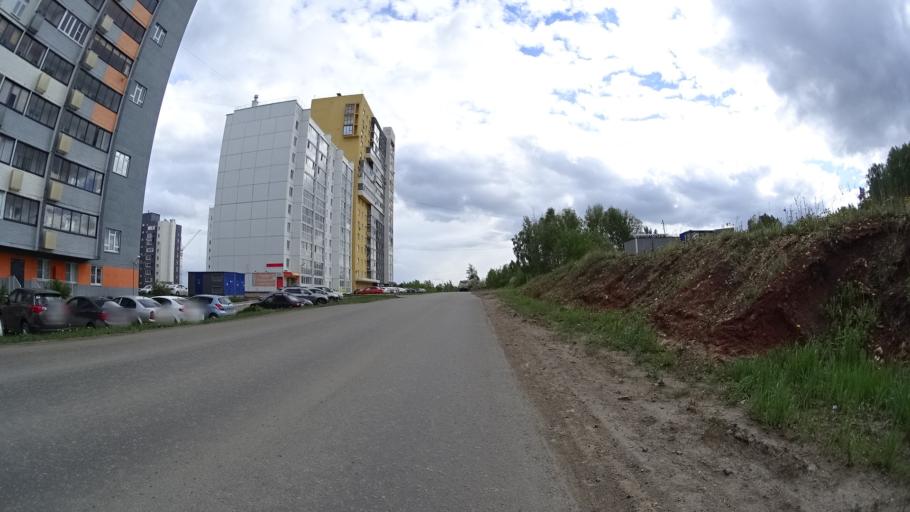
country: RU
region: Chelyabinsk
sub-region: Gorod Chelyabinsk
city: Chelyabinsk
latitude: 55.1612
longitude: 61.2857
